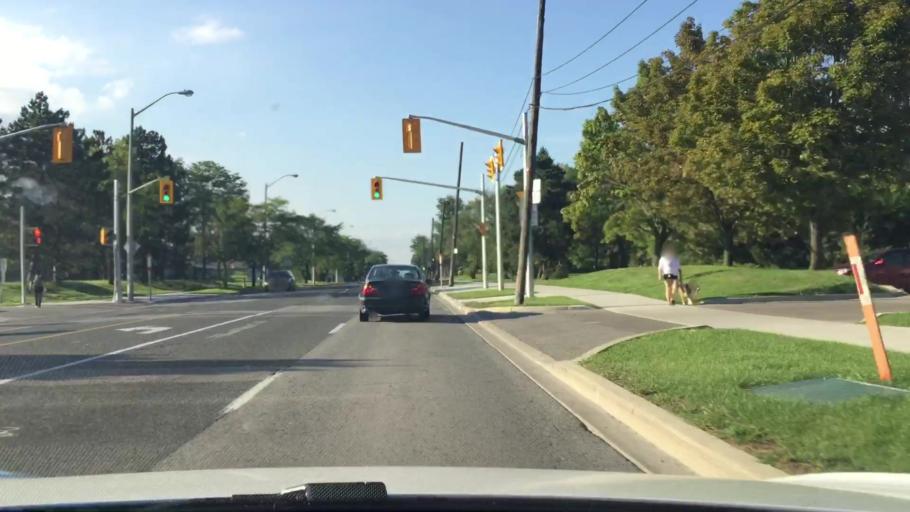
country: CA
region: Ontario
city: Scarborough
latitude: 43.8025
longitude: -79.3083
